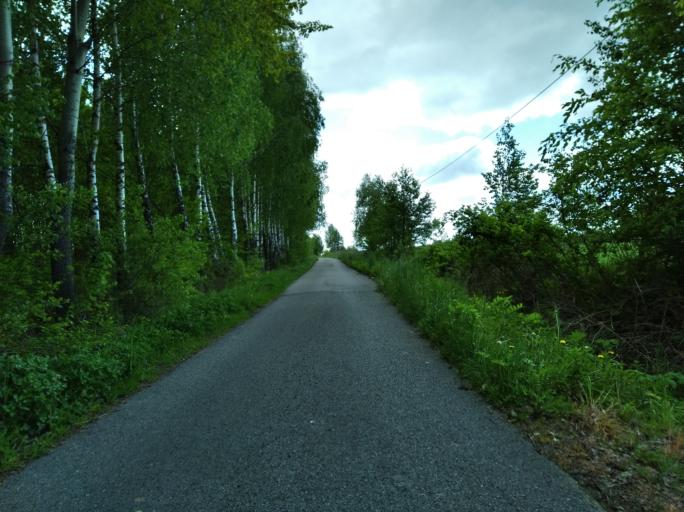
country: PL
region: Subcarpathian Voivodeship
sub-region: Powiat ropczycko-sedziszowski
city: Wielopole Skrzynskie
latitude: 49.9293
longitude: 21.6230
